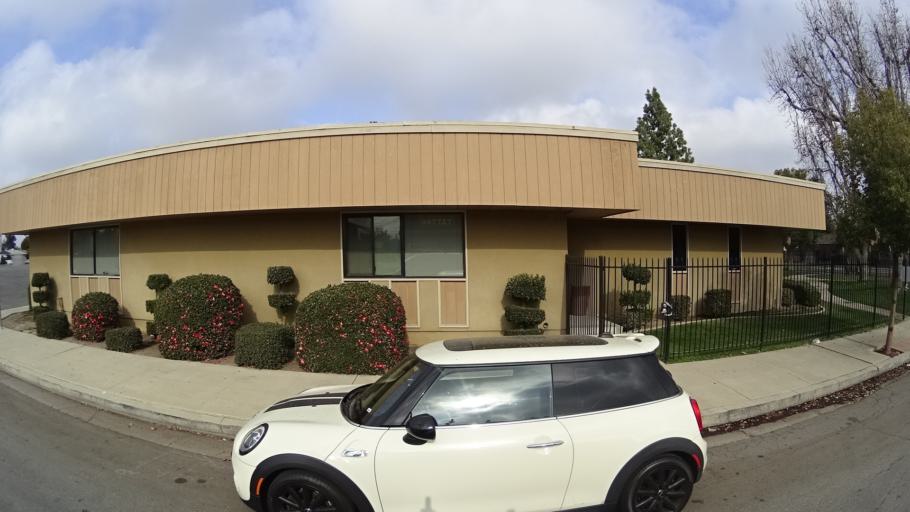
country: US
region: California
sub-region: Kern County
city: Bakersfield
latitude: 35.3830
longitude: -119.0239
